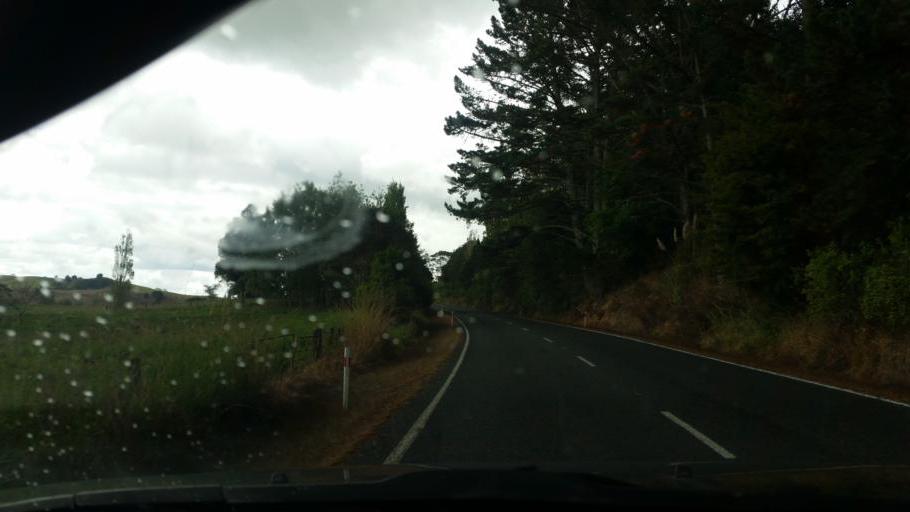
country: NZ
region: Northland
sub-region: Whangarei
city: Ruakaka
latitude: -35.9488
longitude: 174.2938
